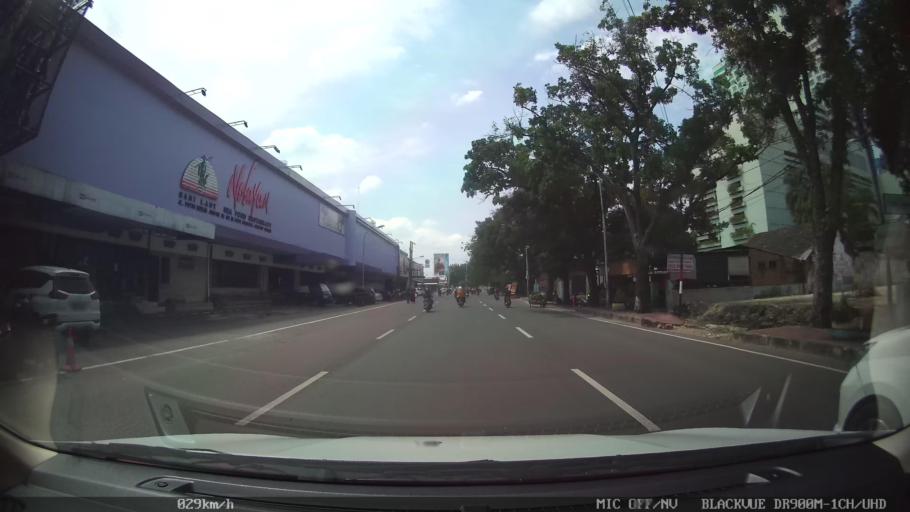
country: ID
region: North Sumatra
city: Medan
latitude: 3.5982
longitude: 98.6764
